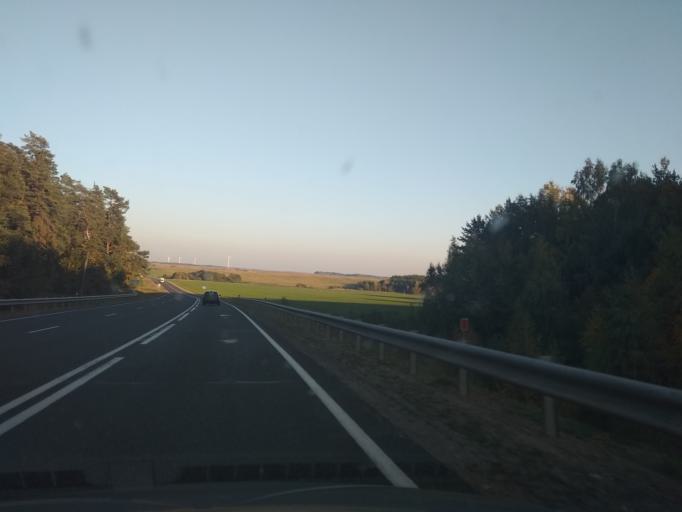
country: BY
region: Grodnenskaya
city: Zel'va
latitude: 53.1376
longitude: 24.7152
